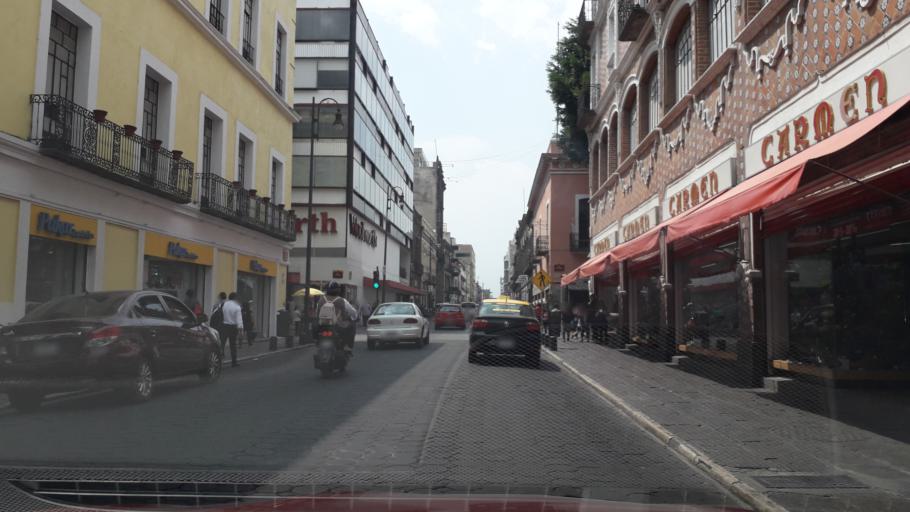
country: MX
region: Puebla
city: Puebla
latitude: 19.0450
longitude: -98.1978
